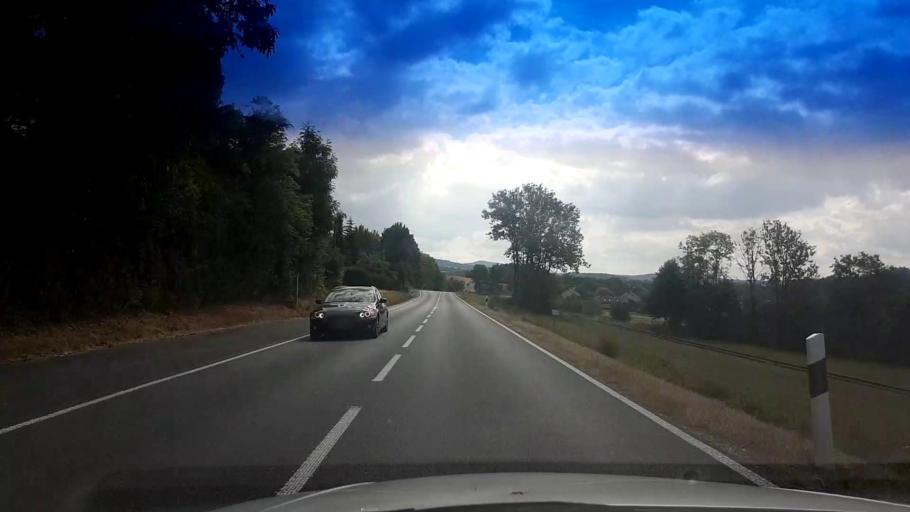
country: DE
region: Bavaria
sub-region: Upper Franconia
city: Reuth
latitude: 49.9734
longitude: 11.6813
